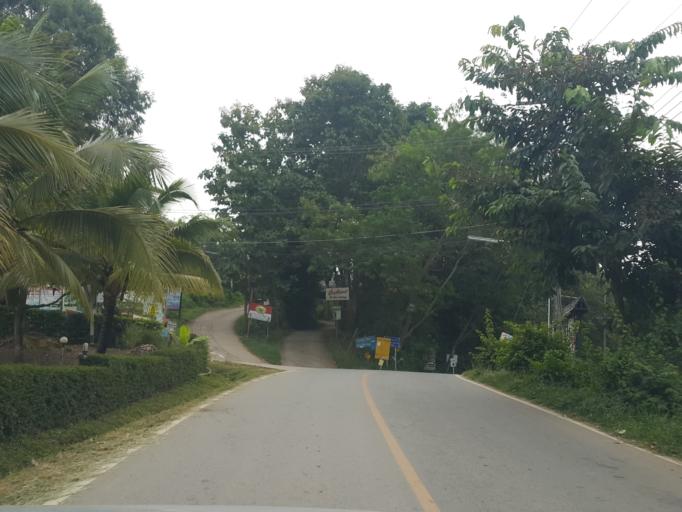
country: TH
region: Chiang Mai
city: Pai
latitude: 19.3557
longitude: 98.4458
